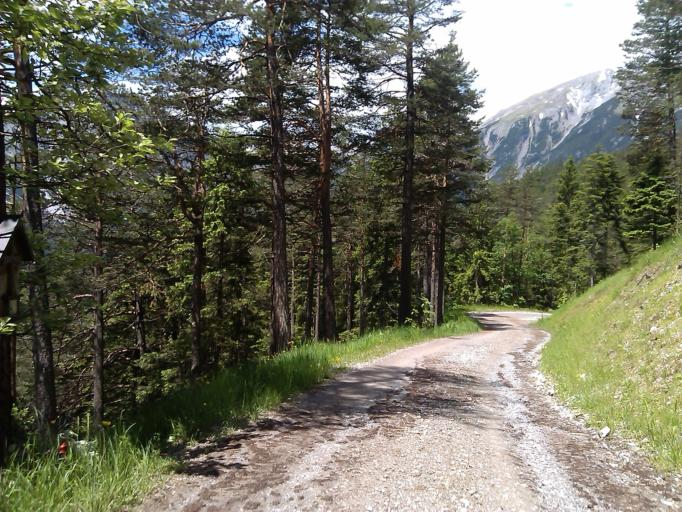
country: AT
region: Tyrol
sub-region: Politischer Bezirk Imst
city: Nassereith
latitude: 47.3544
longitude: 10.8445
